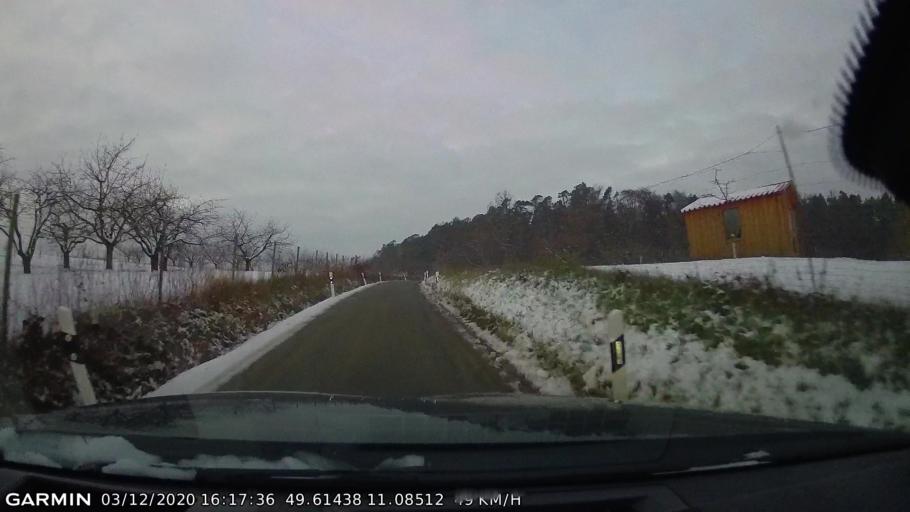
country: DE
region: Bavaria
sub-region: Regierungsbezirk Mittelfranken
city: Uttenreuth
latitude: 49.6145
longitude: 11.0851
